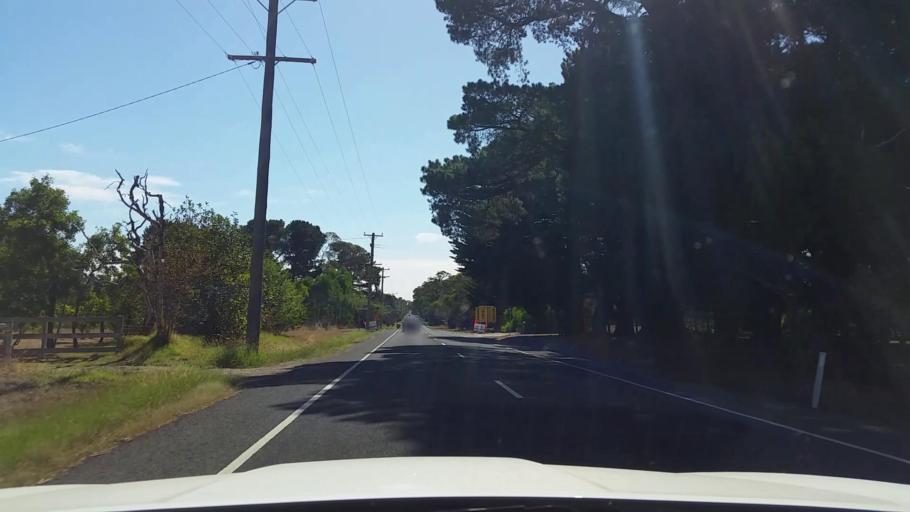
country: AU
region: Victoria
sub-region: Mornington Peninsula
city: Tyabb
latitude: -38.2557
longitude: 145.1463
